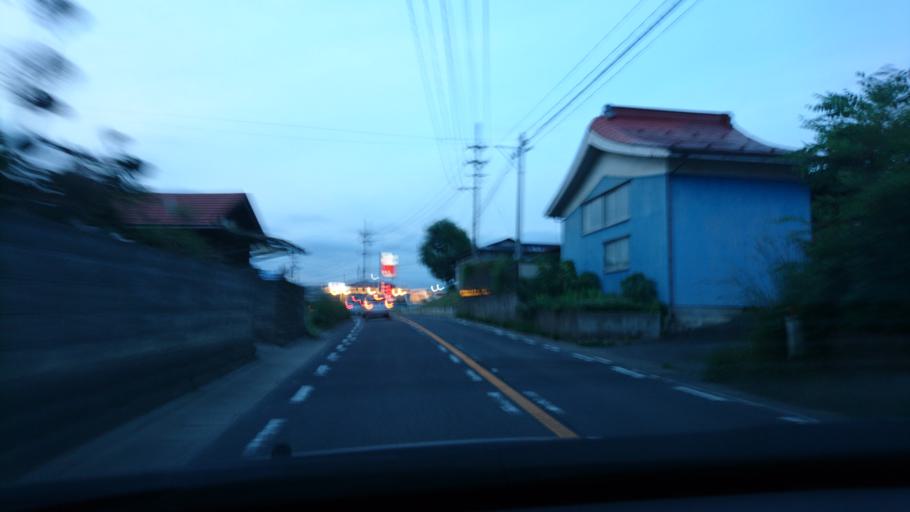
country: JP
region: Iwate
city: Ichinoseki
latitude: 38.8154
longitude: 140.9858
